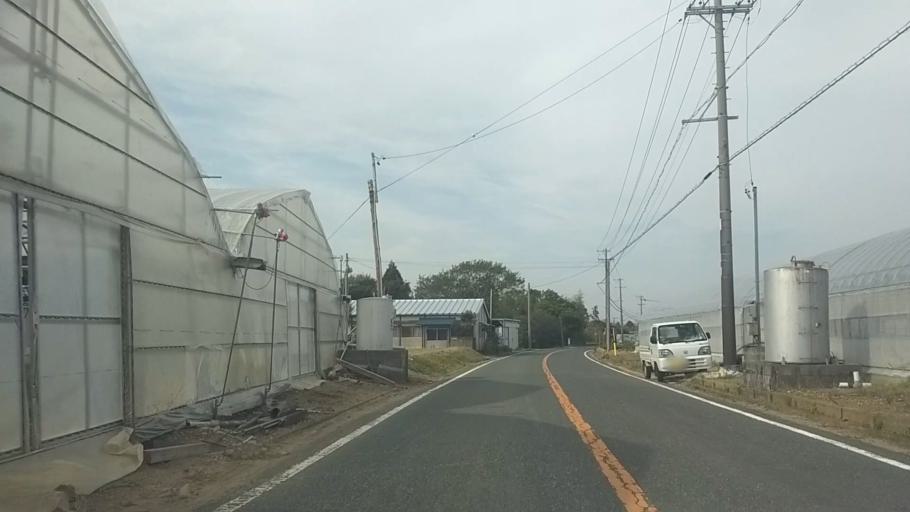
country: JP
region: Shizuoka
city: Hamamatsu
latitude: 34.7104
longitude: 137.6417
